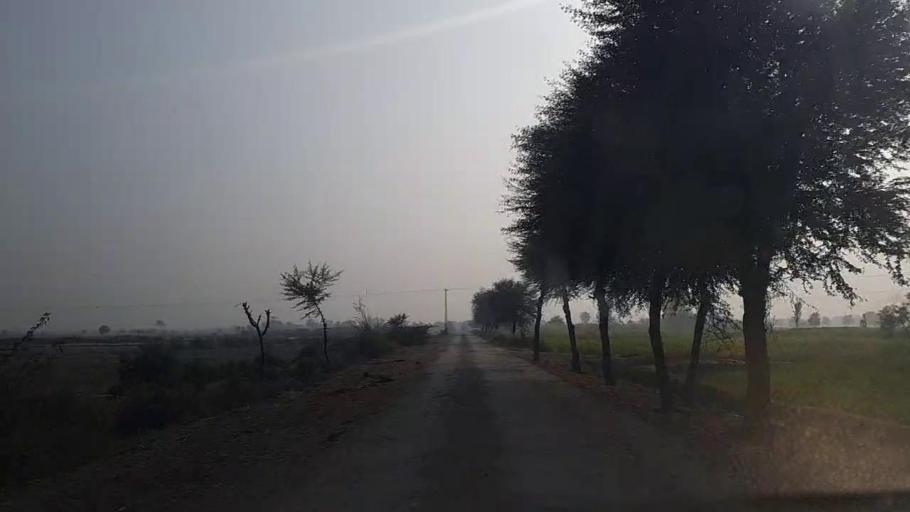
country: PK
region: Sindh
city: Sanghar
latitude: 26.0846
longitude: 68.8765
